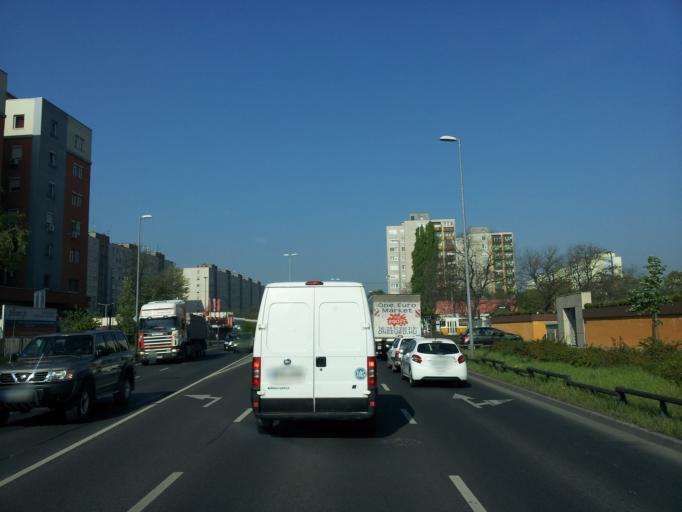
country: HU
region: Budapest
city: Budapest XI. keruelet
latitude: 47.4558
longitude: 19.0411
